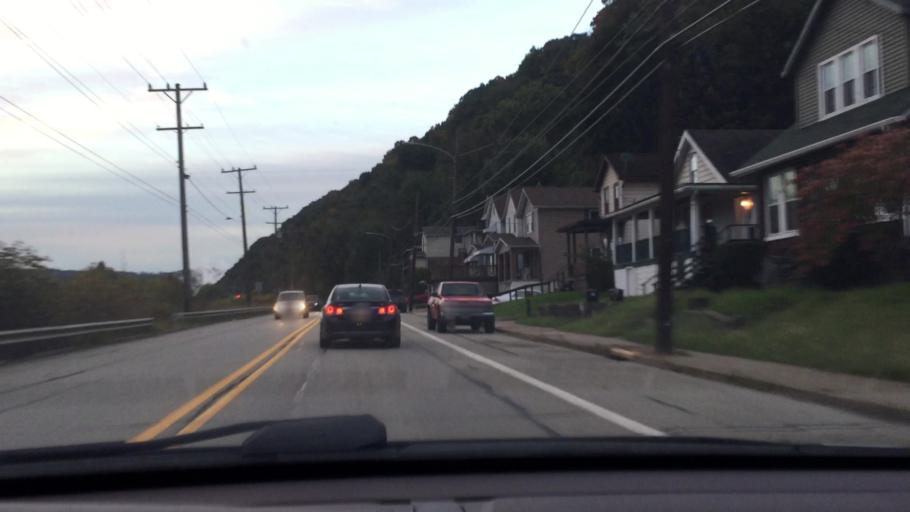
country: US
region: Pennsylvania
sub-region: Westmoreland County
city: New Kensington
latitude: 40.5694
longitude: -79.7766
